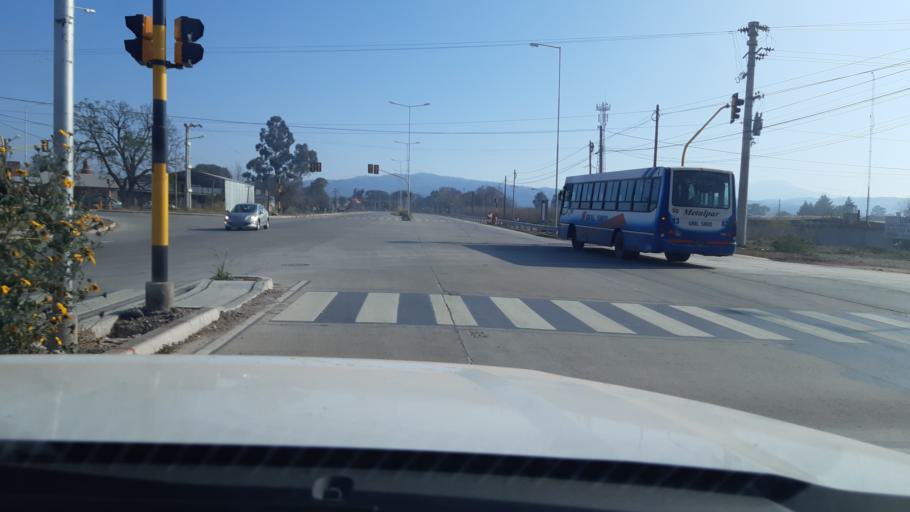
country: AR
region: Jujuy
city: Palpala
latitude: -24.2325
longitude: -65.2325
